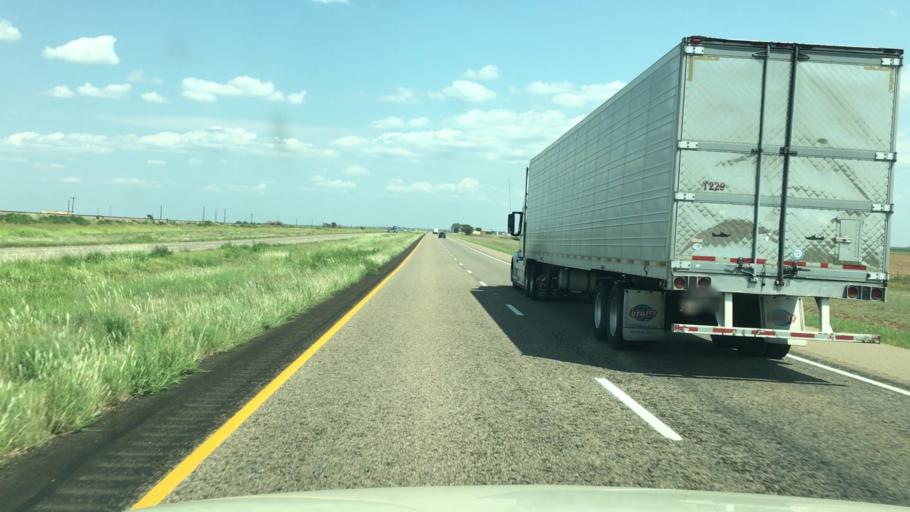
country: US
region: Texas
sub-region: Armstrong County
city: Claude
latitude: 35.0320
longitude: -101.1300
